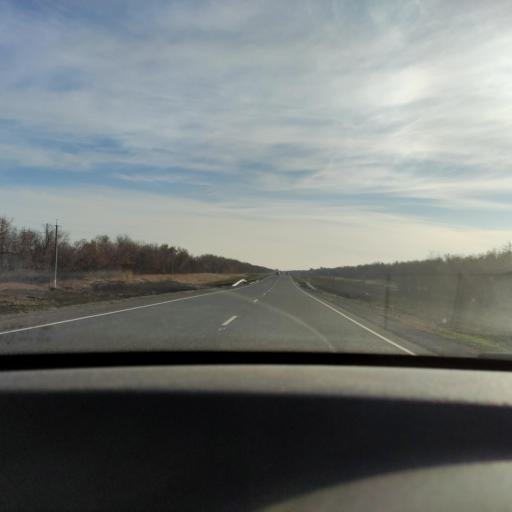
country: RU
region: Samara
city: Krasnoarmeyskoye
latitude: 52.8050
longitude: 50.0133
